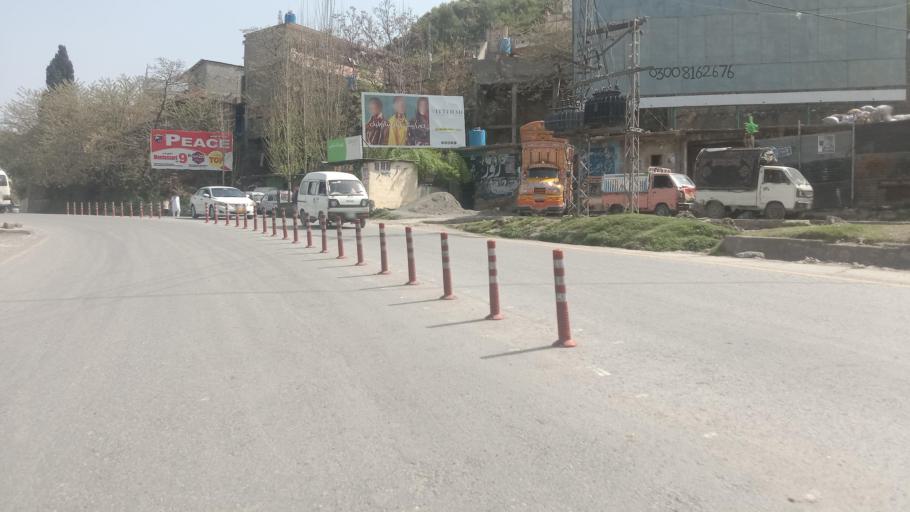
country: PK
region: Khyber Pakhtunkhwa
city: Abbottabad
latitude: 34.1350
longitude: 73.2061
